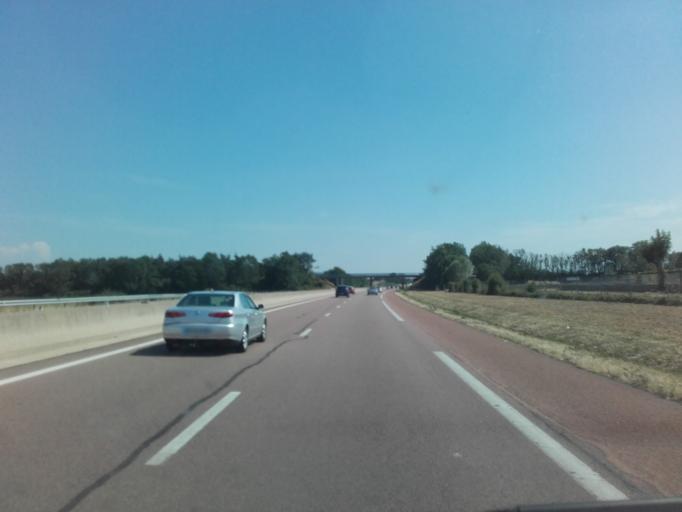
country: FR
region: Bourgogne
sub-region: Departement de la Cote-d'Or
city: Pouilly-en-Auxois
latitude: 47.2436
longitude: 4.5759
